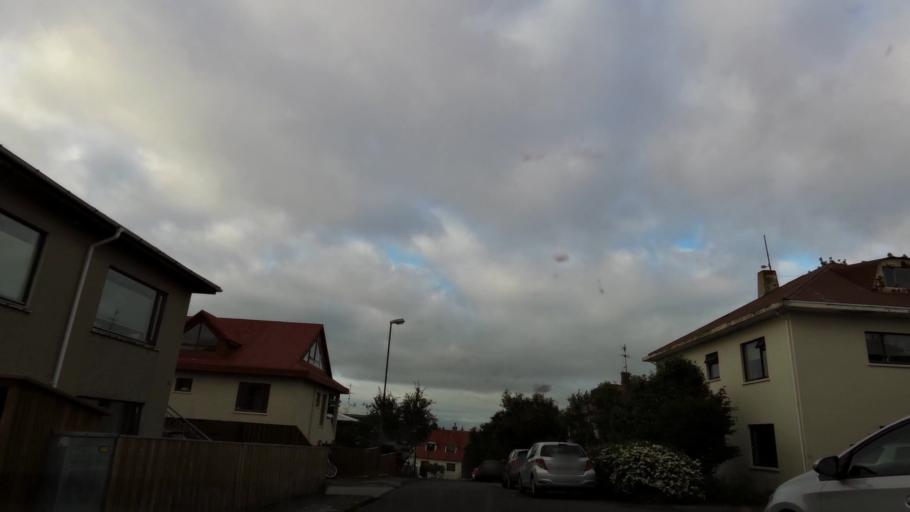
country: IS
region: Capital Region
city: Hafnarfjoerdur
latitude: 64.0642
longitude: -21.9469
